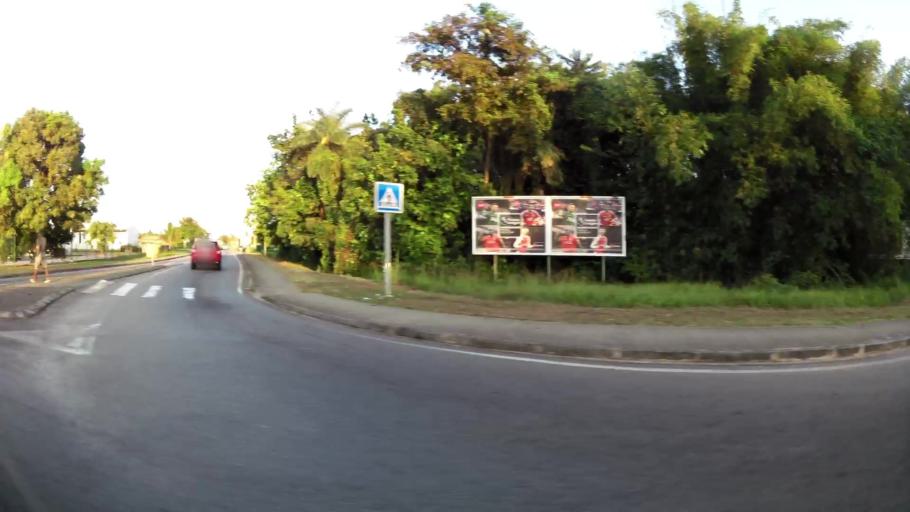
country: GF
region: Guyane
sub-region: Guyane
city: Cayenne
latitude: 4.9293
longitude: -52.3031
